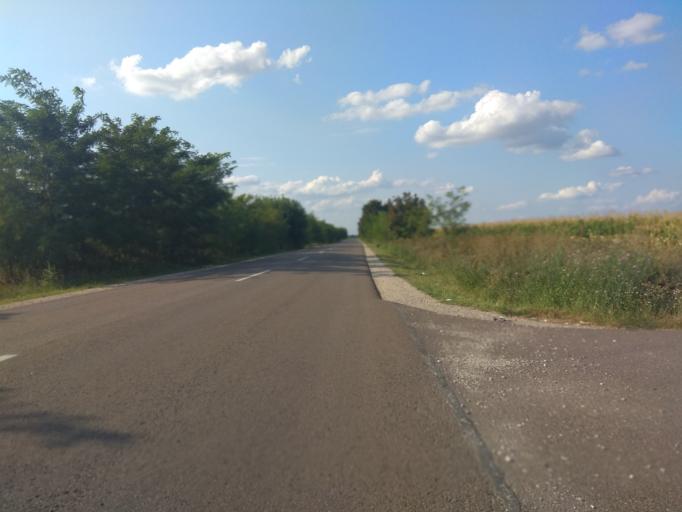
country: HU
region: Borsod-Abauj-Zemplen
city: Hejobaba
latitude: 47.9133
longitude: 20.8839
